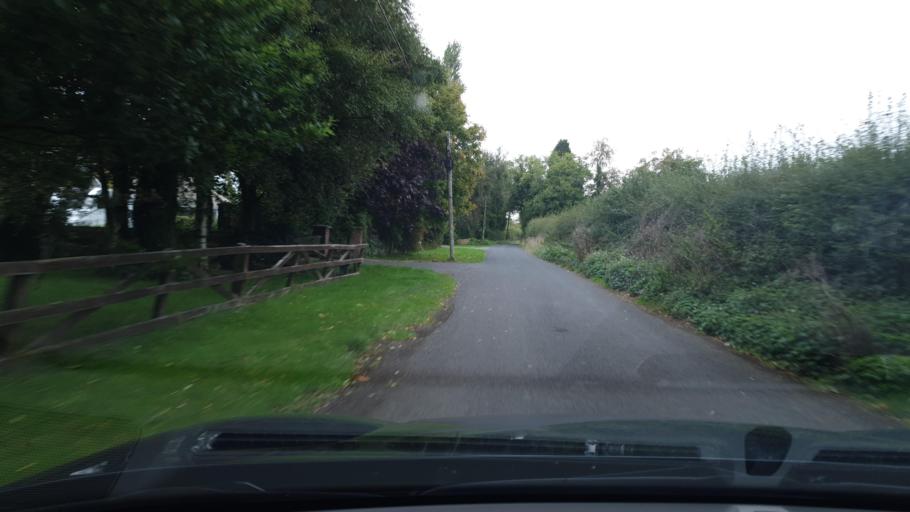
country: IE
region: Leinster
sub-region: An Mhi
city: Dunshaughlin
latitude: 53.5540
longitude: -6.5184
